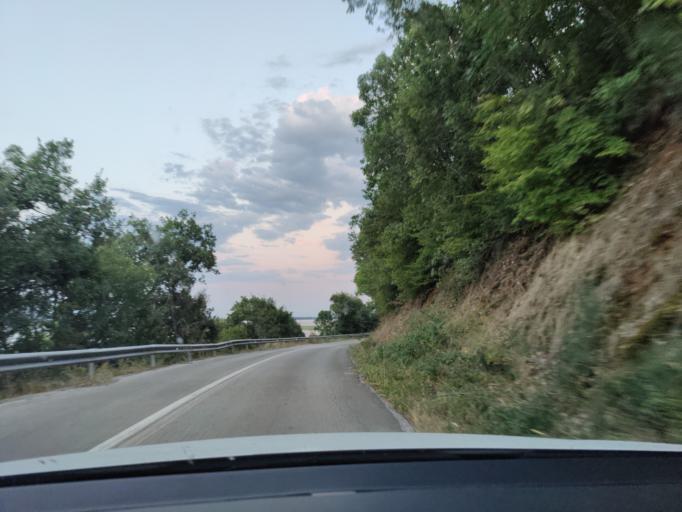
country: GR
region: Central Macedonia
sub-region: Nomos Serron
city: Chrysochorafa
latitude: 41.1694
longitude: 23.1773
